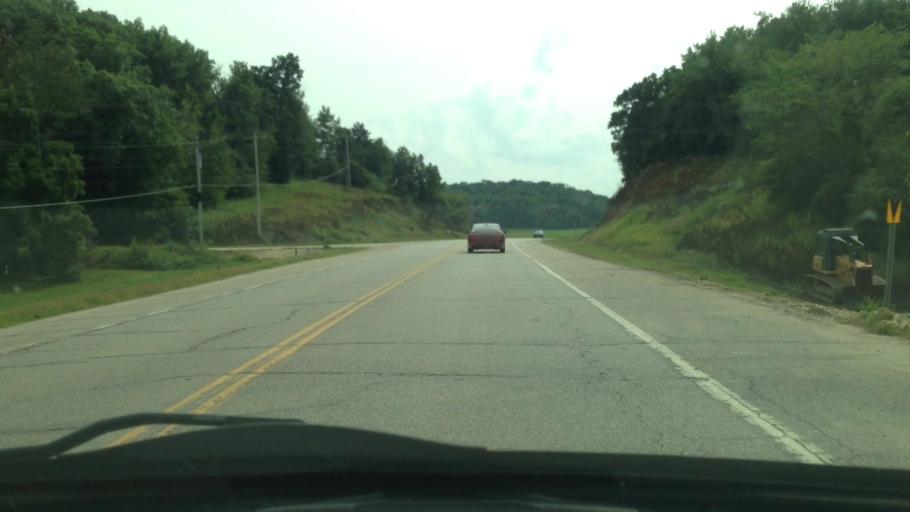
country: US
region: Minnesota
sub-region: Olmsted County
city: Rochester
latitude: 44.0927
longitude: -92.4412
